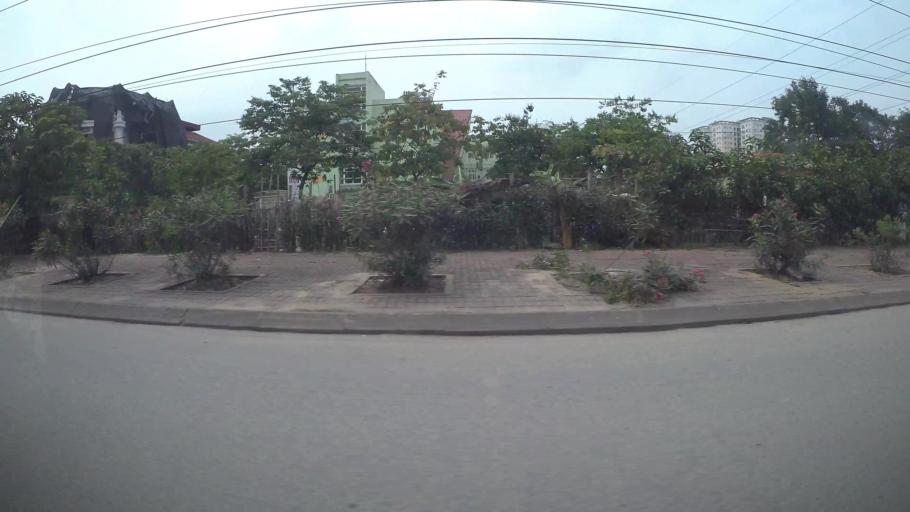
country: VN
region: Ha Noi
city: Trau Quy
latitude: 21.0654
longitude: 105.9053
